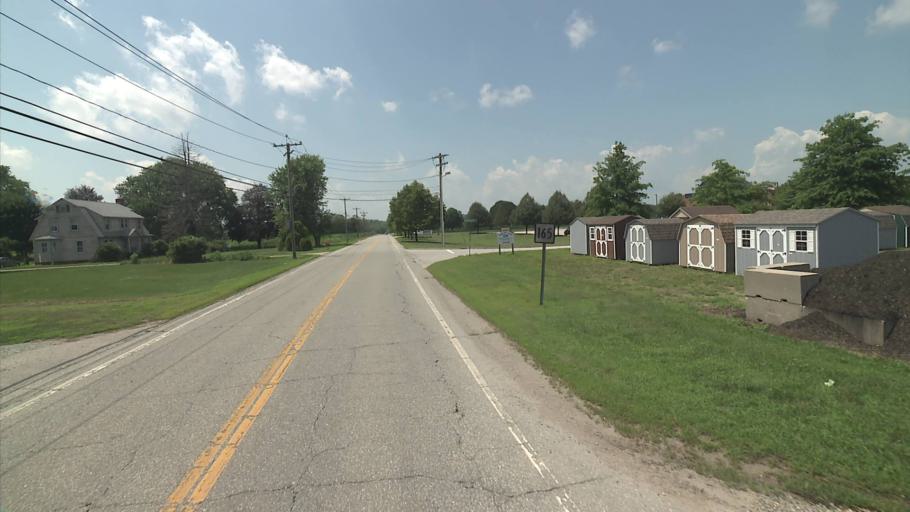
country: US
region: Connecticut
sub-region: New London County
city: Preston City
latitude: 41.5285
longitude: -71.9833
